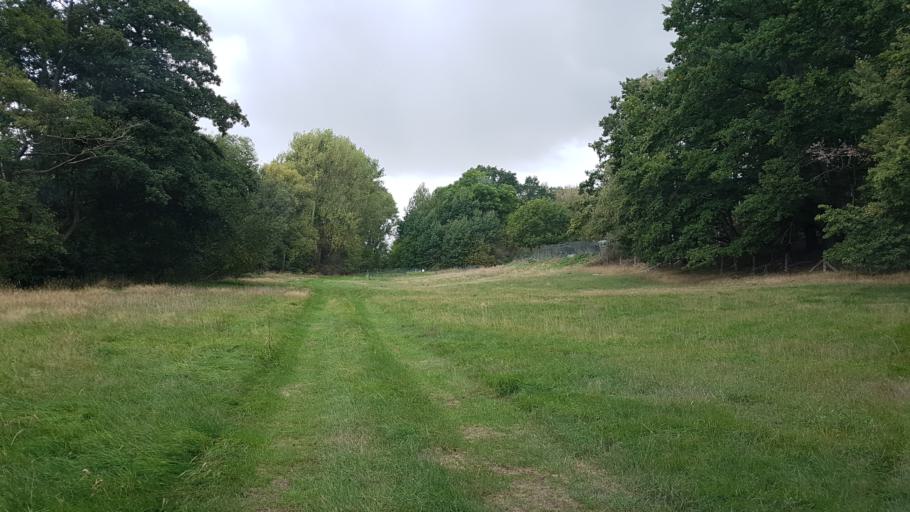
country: DE
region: Saxony
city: Dahlen
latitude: 51.3671
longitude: 13.0129
